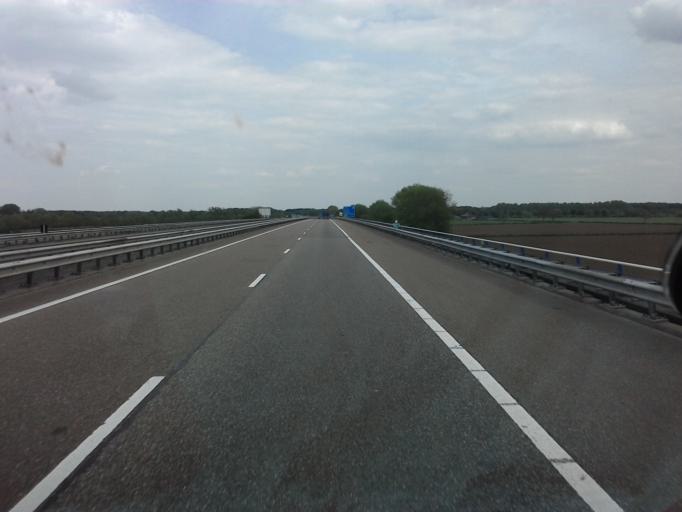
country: NL
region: North Brabant
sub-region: Gemeente Boxmeer
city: Boxmeer
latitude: 51.6635
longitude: 5.9635
